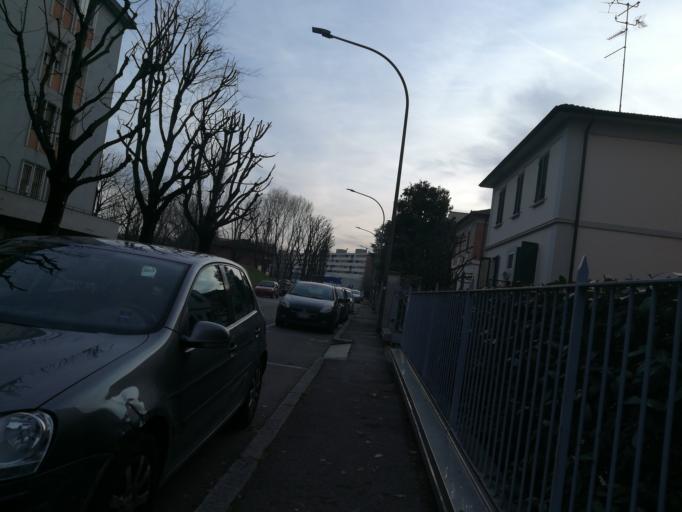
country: IT
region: Emilia-Romagna
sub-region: Provincia di Bologna
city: Progresso
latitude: 44.5462
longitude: 11.3553
